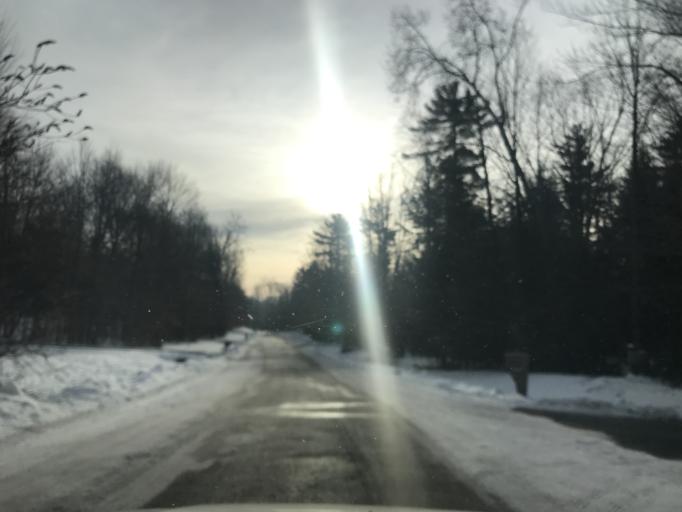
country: US
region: Wisconsin
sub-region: Brown County
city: Suamico
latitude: 44.6879
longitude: -88.0631
